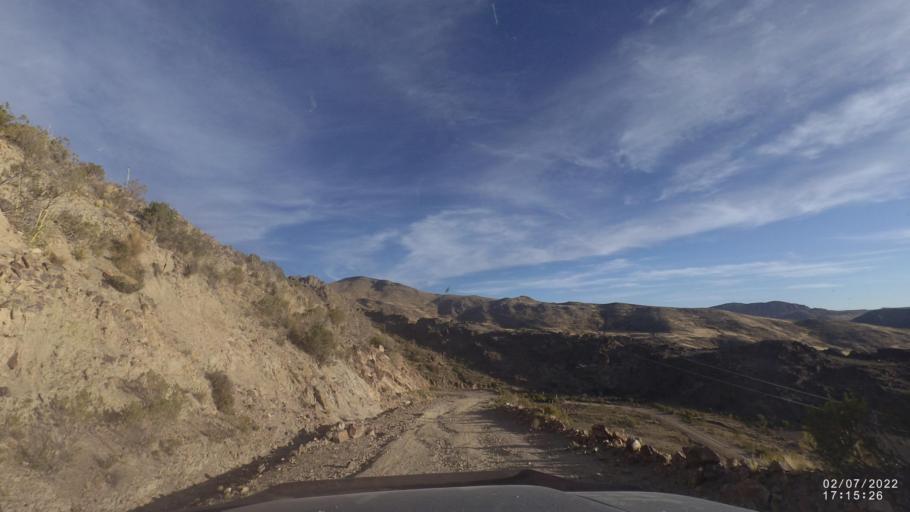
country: BO
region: Cochabamba
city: Irpa Irpa
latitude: -17.8761
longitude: -66.5835
